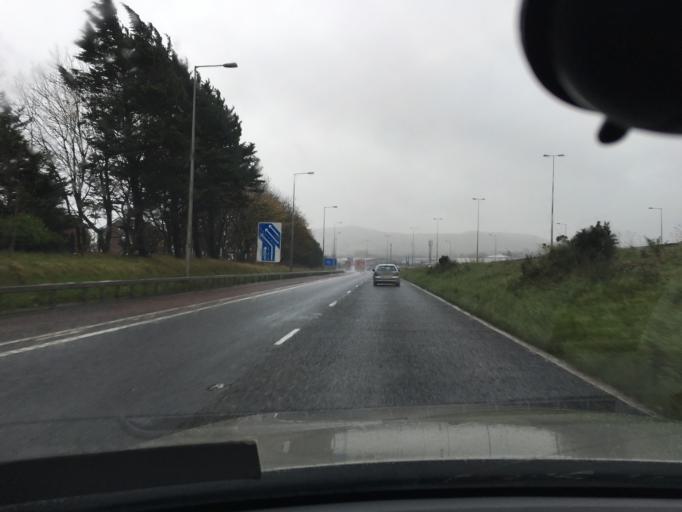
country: GB
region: Northern Ireland
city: Carnmoney
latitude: 54.6755
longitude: -5.9762
